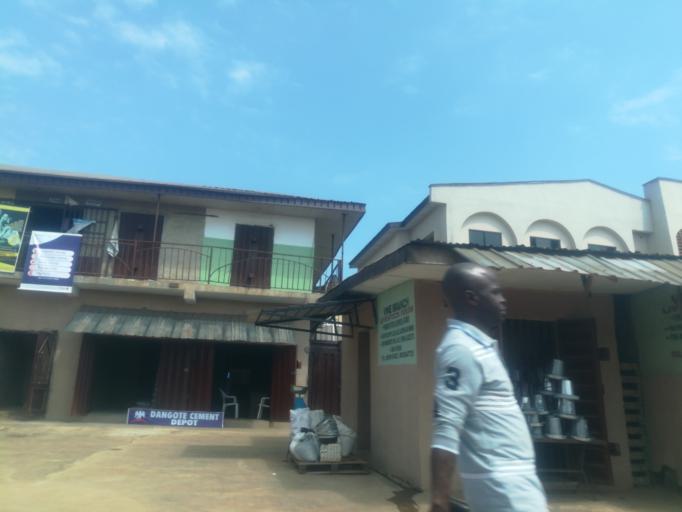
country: NG
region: Oyo
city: Egbeda
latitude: 7.4213
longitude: 3.9782
